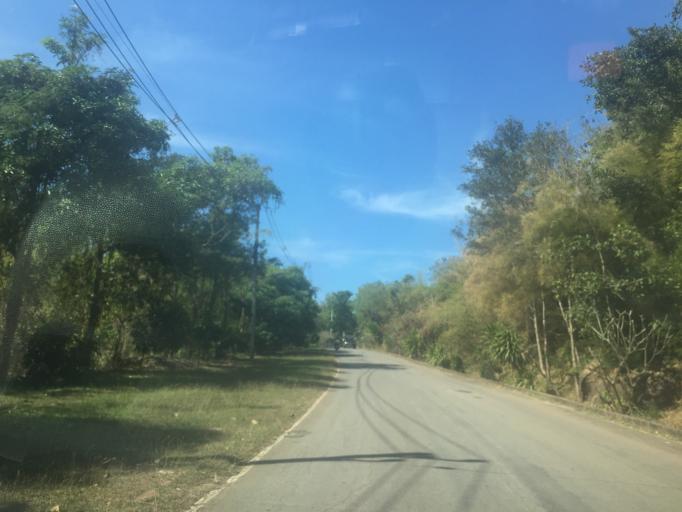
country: TH
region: Changwat Nong Bua Lamphu
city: Nong Bua Lamphu
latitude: 17.2440
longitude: 102.5188
